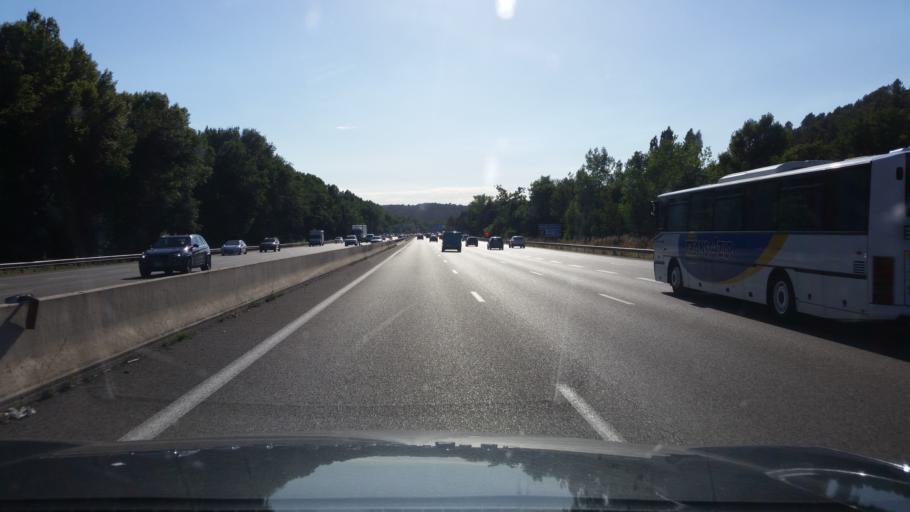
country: FR
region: Provence-Alpes-Cote d'Azur
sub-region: Departement des Bouches-du-Rhone
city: Chateauneuf-le-Rouge
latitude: 43.4816
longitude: 5.5561
